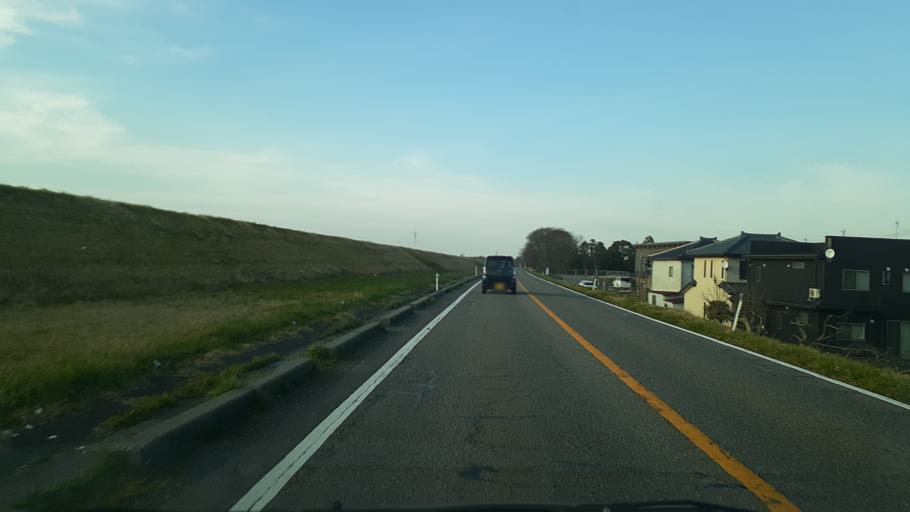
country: JP
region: Niigata
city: Niigata-shi
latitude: 37.8585
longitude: 139.0246
